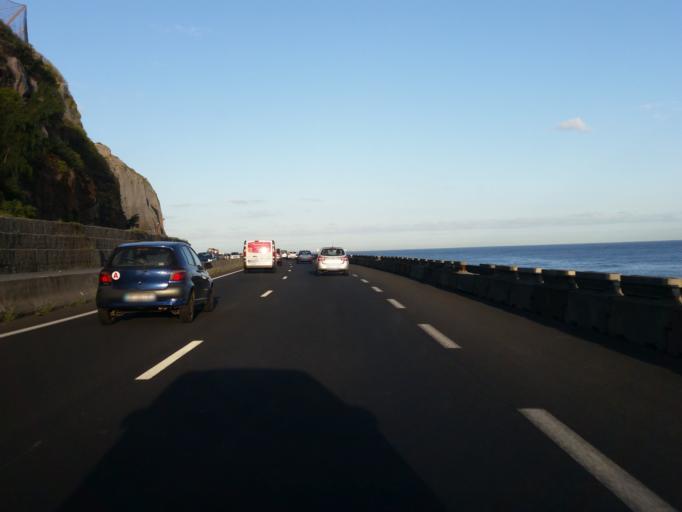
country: RE
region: Reunion
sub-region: Reunion
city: La Possession
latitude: -20.8916
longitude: 55.3819
